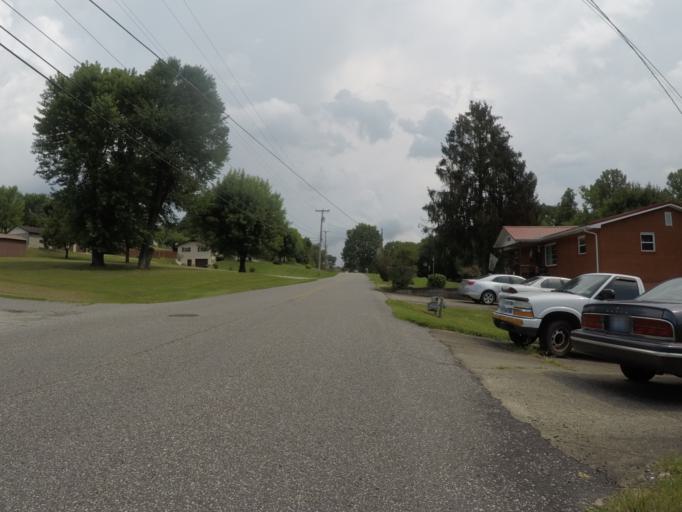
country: US
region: Kentucky
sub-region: Boyd County
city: Meads
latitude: 38.4339
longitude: -82.7086
